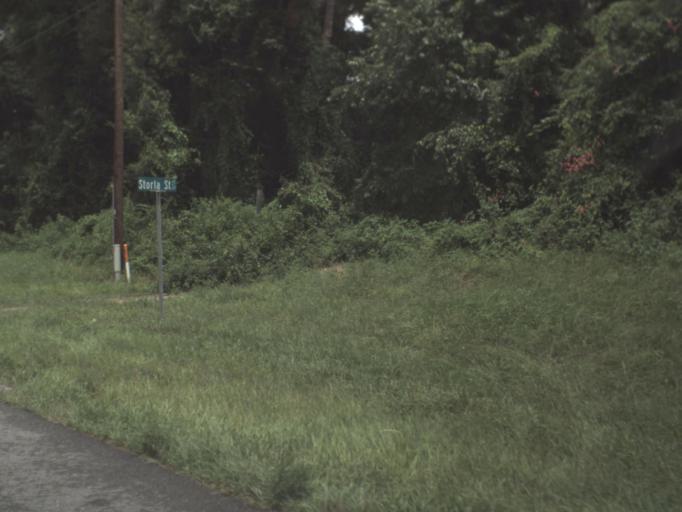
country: US
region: Florida
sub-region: Hernando County
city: Ridge Manor
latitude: 28.5691
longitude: -82.1559
